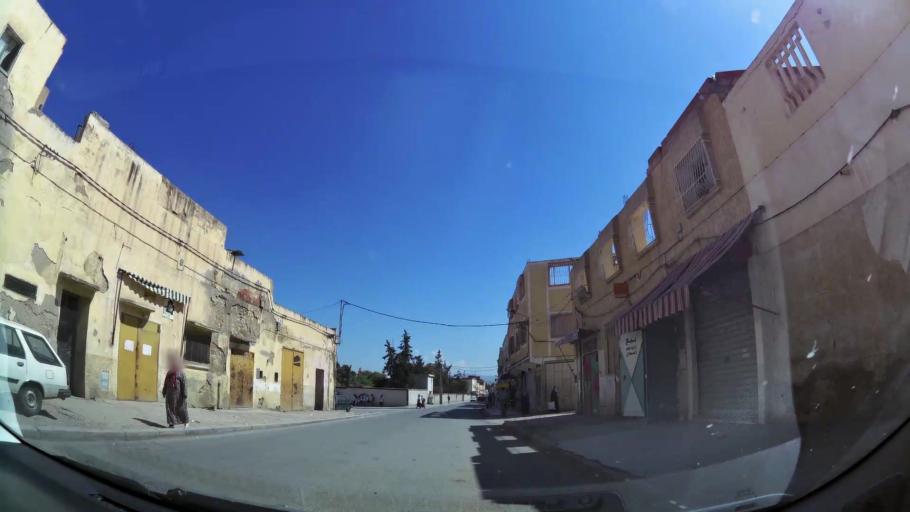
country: MA
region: Oriental
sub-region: Oujda-Angad
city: Oujda
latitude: 34.6843
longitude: -1.9322
